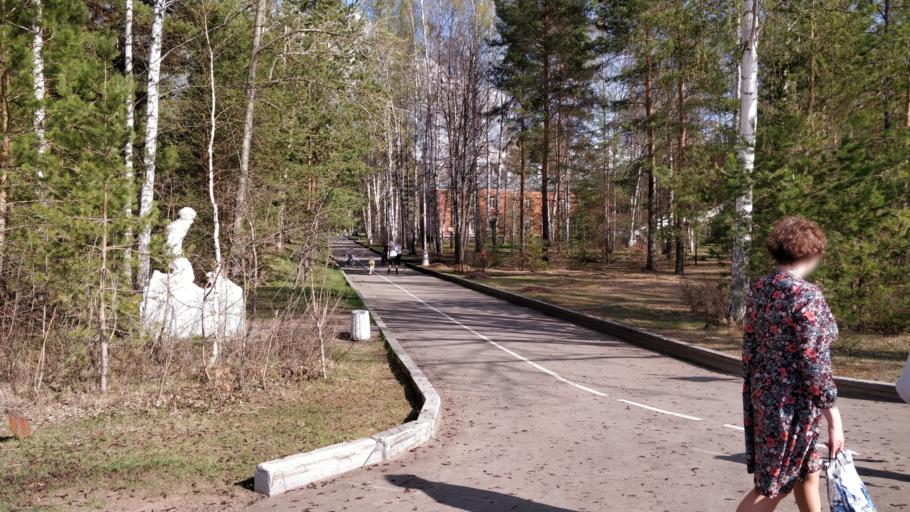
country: RU
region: Perm
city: Ust'-Kachka
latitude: 58.0112
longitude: 55.6687
